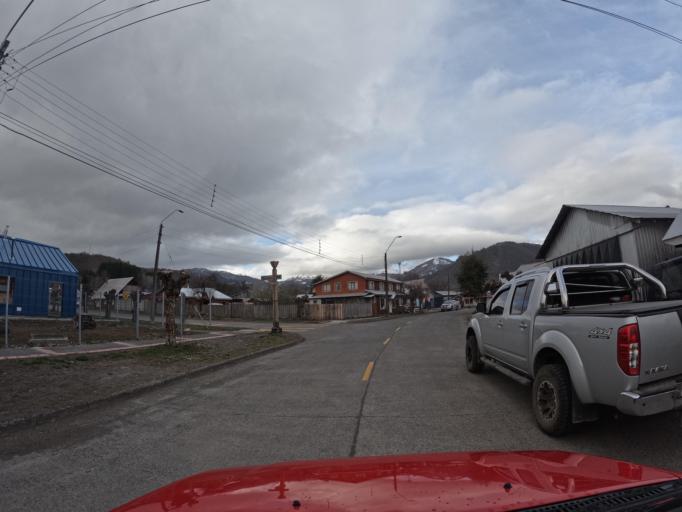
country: AR
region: Neuquen
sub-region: Departamento de Loncopue
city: Loncopue
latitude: -38.4506
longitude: -71.3729
